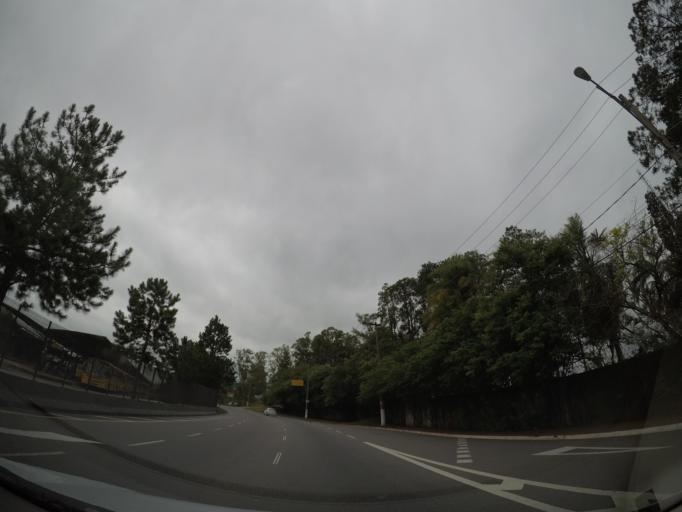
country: BR
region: Sao Paulo
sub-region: Jundiai
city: Jundiai
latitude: -23.1449
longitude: -46.9147
